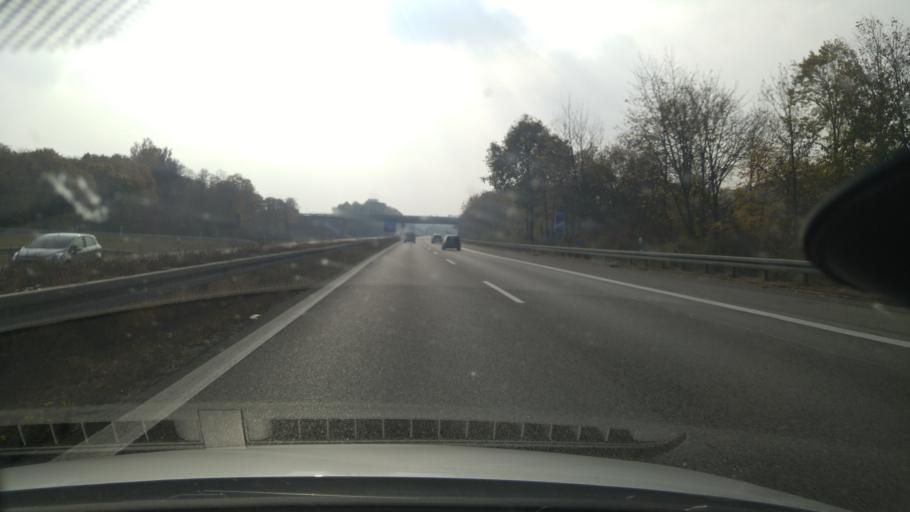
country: DE
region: Baden-Wuerttemberg
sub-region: Karlsruhe Region
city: Empfingen
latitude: 48.4325
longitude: 8.7484
